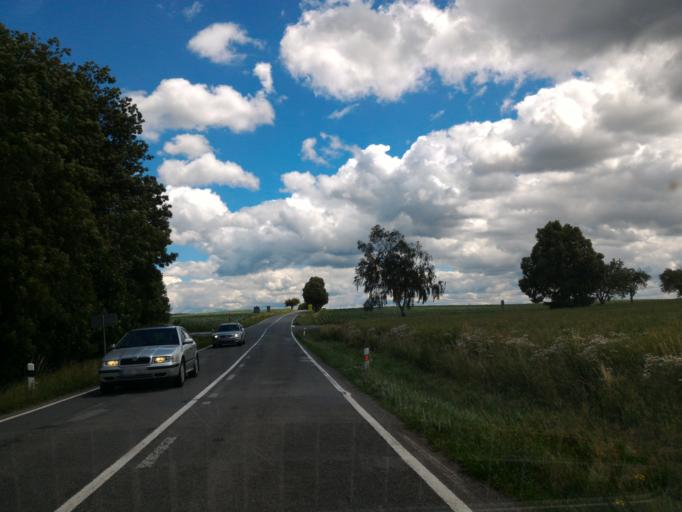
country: CZ
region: Vysocina
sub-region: Okres Jihlava
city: Polna
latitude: 49.4417
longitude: 15.7441
